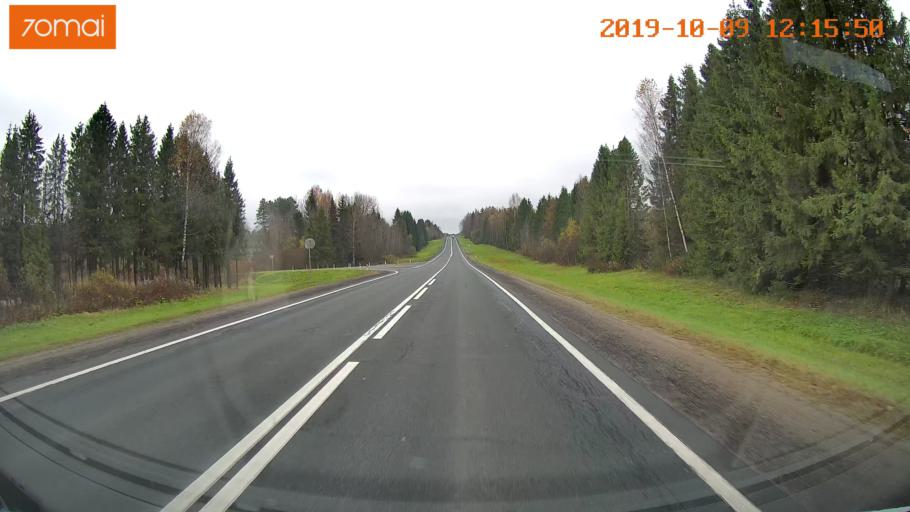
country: RU
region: Jaroslavl
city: Prechistoye
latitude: 58.4775
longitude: 40.3223
